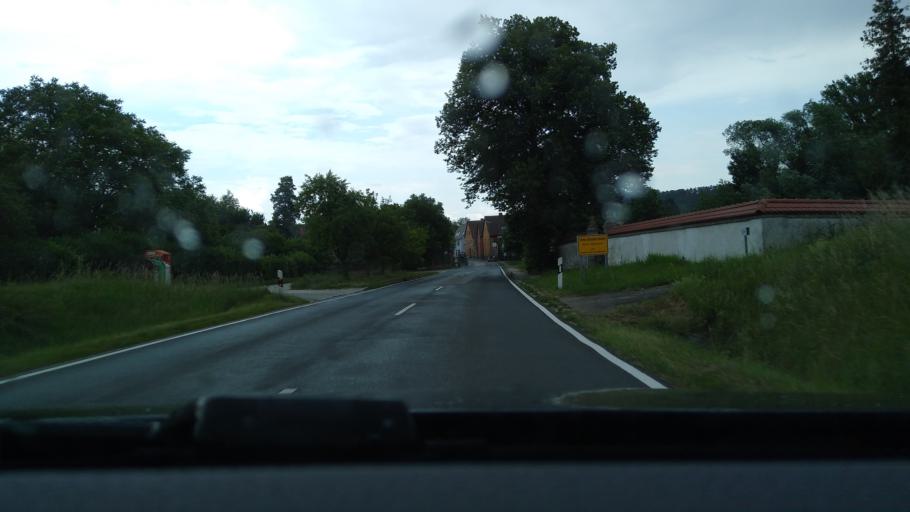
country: DE
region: Bavaria
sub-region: Regierungsbezirk Mittelfranken
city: Flachslanden
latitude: 49.4587
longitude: 10.5333
